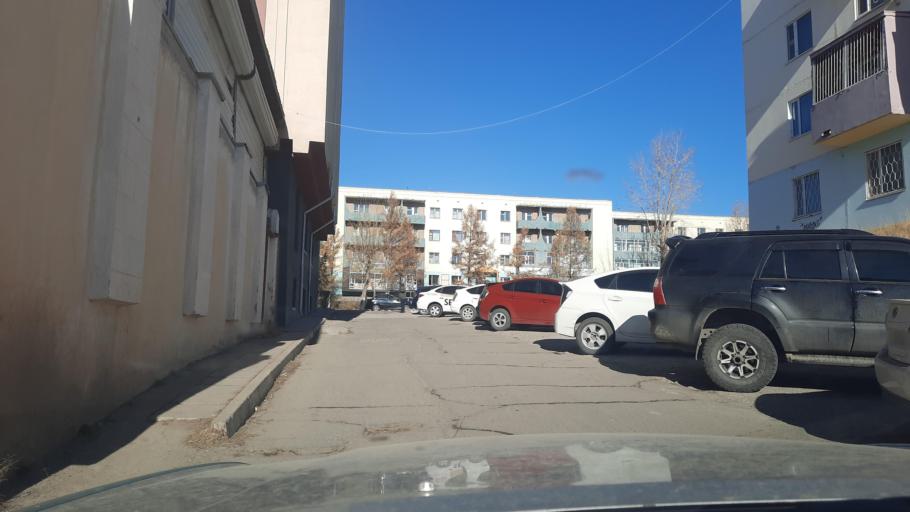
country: MN
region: Orhon
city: Erdenet
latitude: 49.0306
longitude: 104.0573
